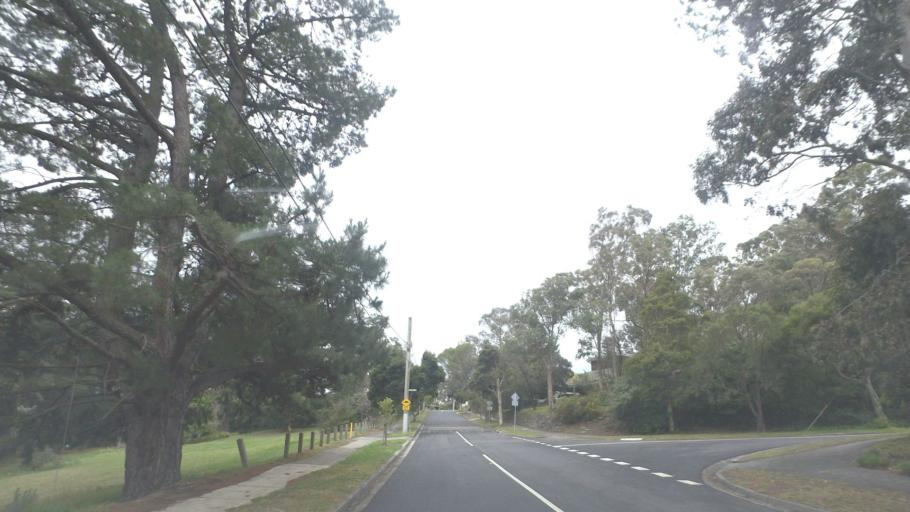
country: AU
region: Victoria
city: Mitcham
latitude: -37.8032
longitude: 145.1950
